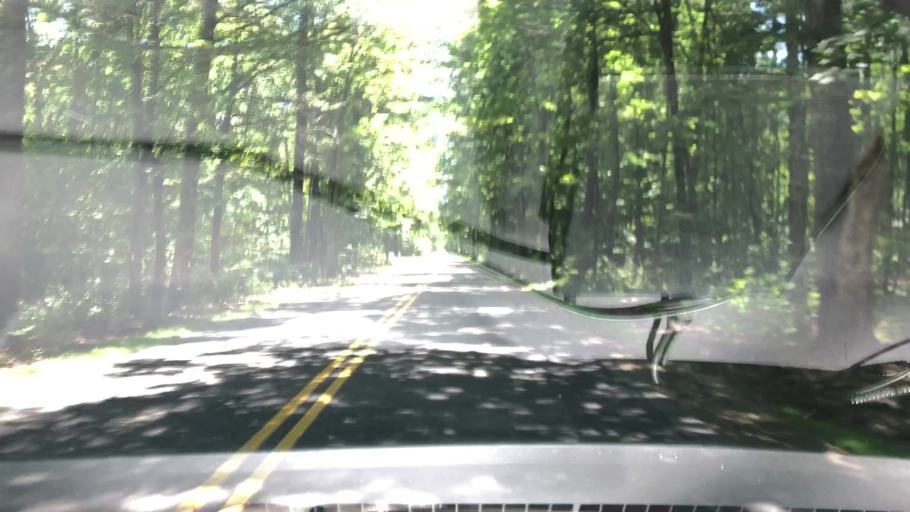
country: US
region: New Hampshire
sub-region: Hillsborough County
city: Milford
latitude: 42.8434
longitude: -71.5802
